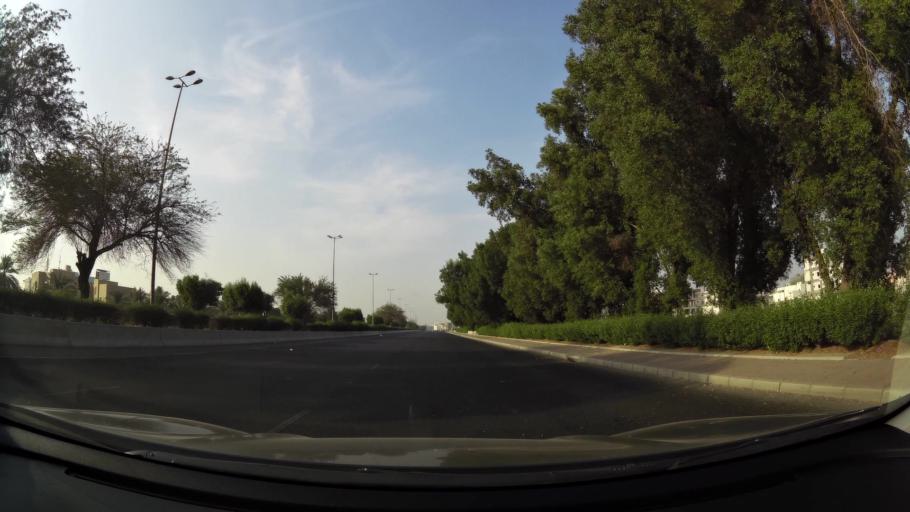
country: KW
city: Al Funaytis
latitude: 29.2152
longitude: 48.0891
